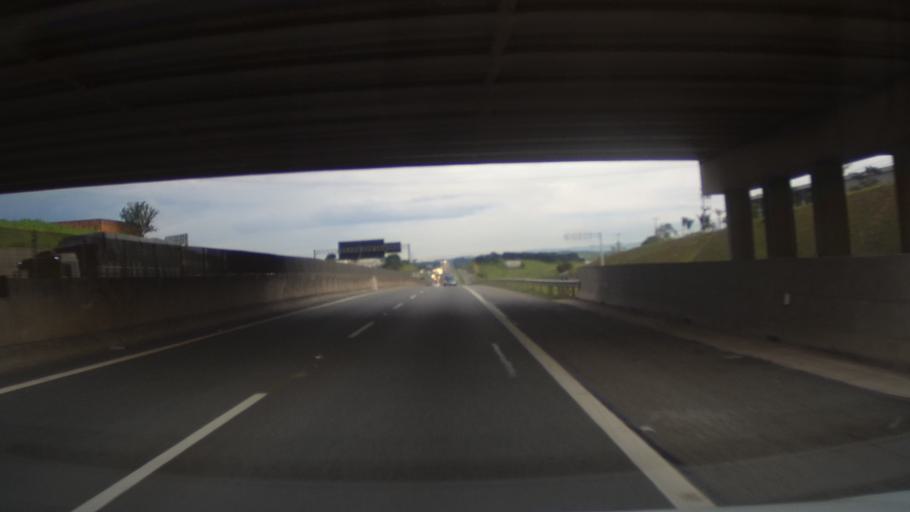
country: BR
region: Sao Paulo
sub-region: Campinas
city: Campinas
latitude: -22.9370
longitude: -47.0700
